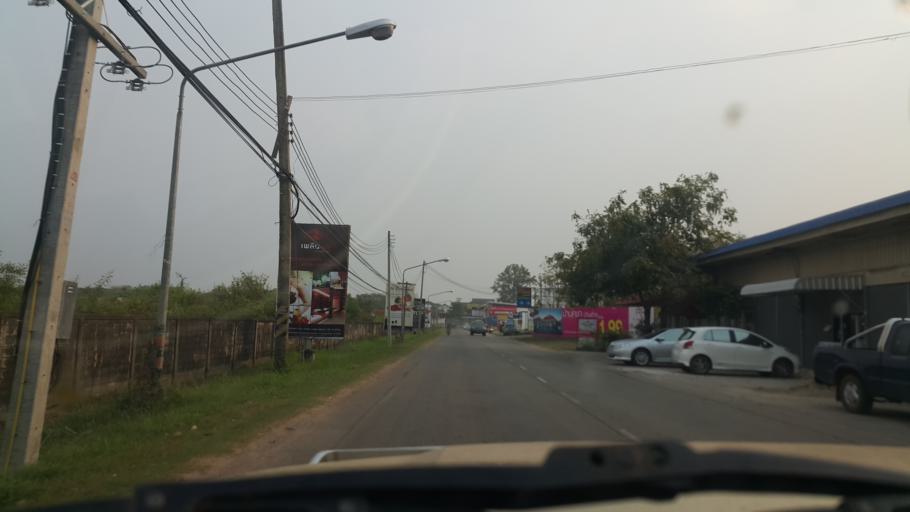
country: TH
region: Changwat Udon Thani
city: Udon Thani
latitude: 17.3965
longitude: 102.7712
